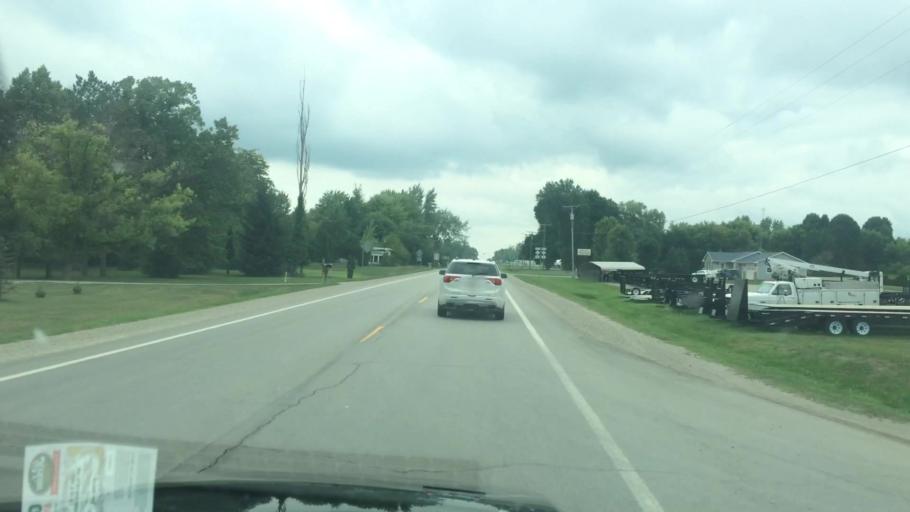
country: US
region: Michigan
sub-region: Tuscola County
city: Cass City
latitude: 43.5993
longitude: -83.0967
